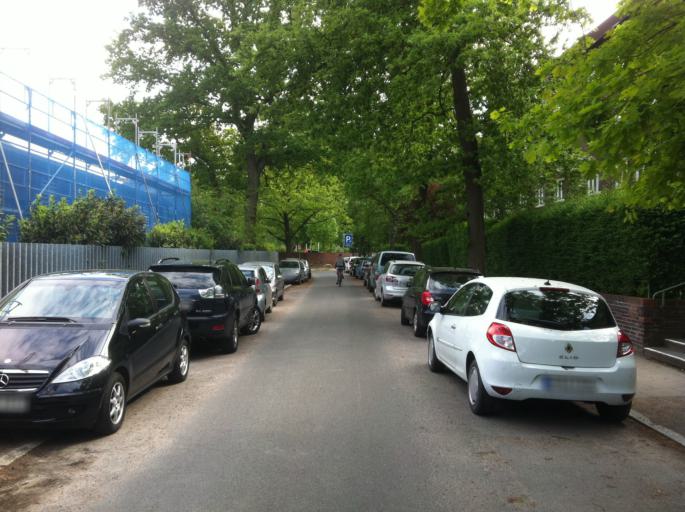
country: DE
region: Hamburg
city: Altona
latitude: 53.5527
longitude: 9.9120
